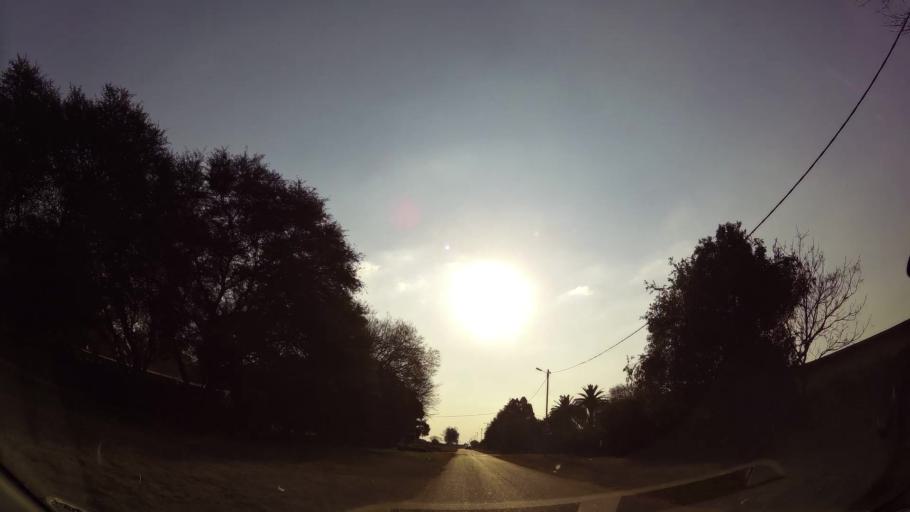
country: ZA
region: Gauteng
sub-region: Ekurhuleni Metropolitan Municipality
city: Benoni
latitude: -26.1479
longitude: 28.3778
